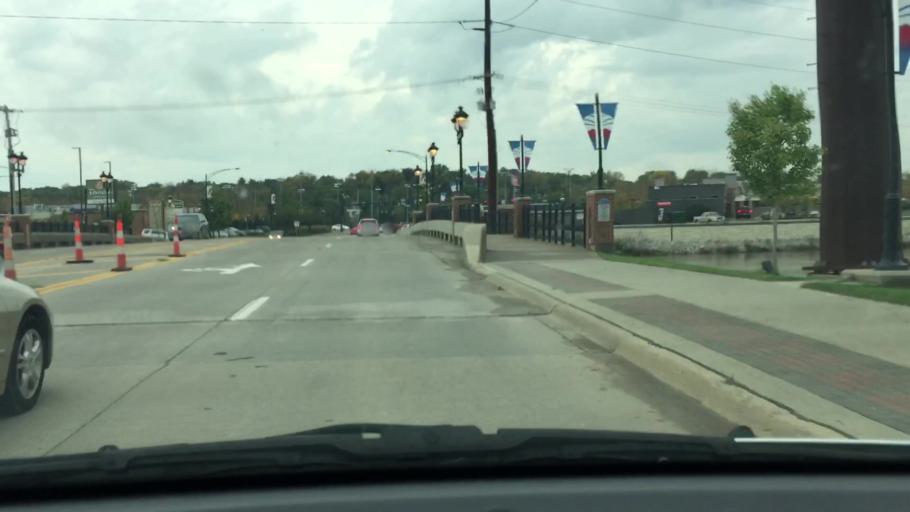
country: US
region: Iowa
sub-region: Johnson County
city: Coralville
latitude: 41.6710
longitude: -91.5656
